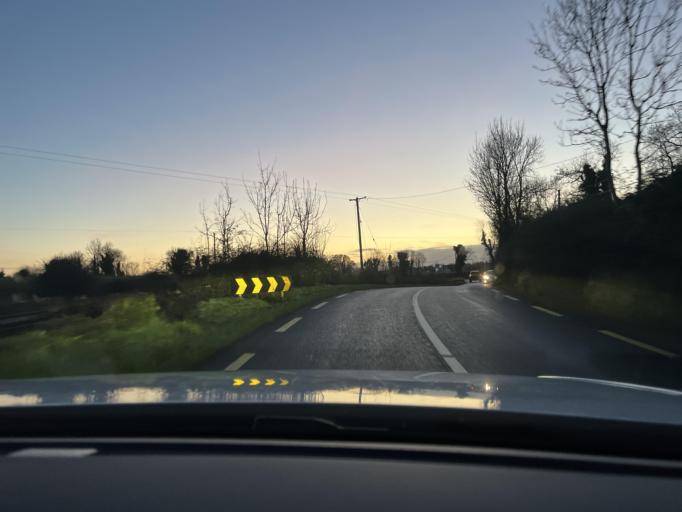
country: IE
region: Connaught
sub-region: County Leitrim
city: Carrick-on-Shannon
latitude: 53.9978
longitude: -8.0283
